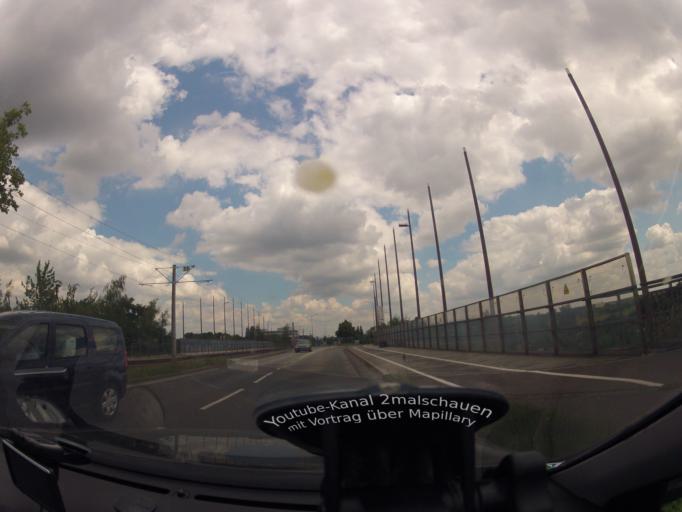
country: DE
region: Saxony
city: Taucha
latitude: 51.3589
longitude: 12.4412
